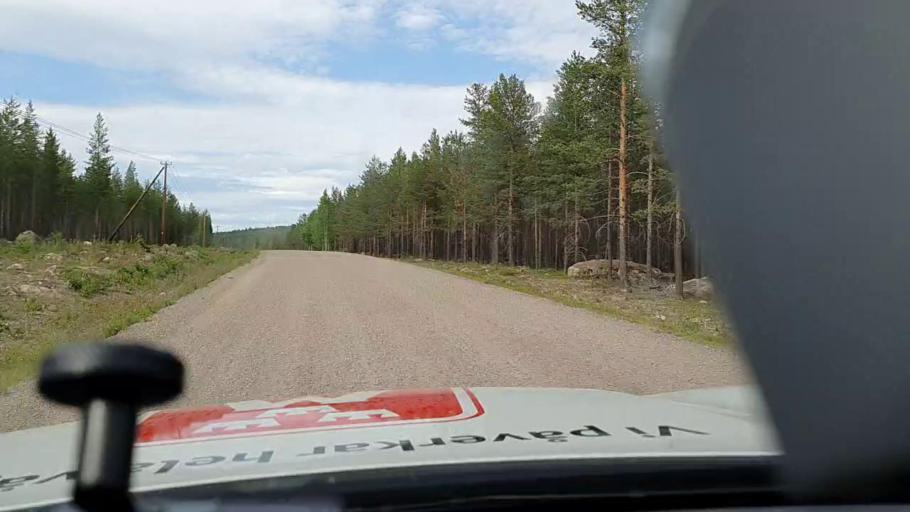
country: SE
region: Norrbotten
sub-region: Alvsbyns Kommun
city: AElvsbyn
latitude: 66.1229
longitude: 20.9931
